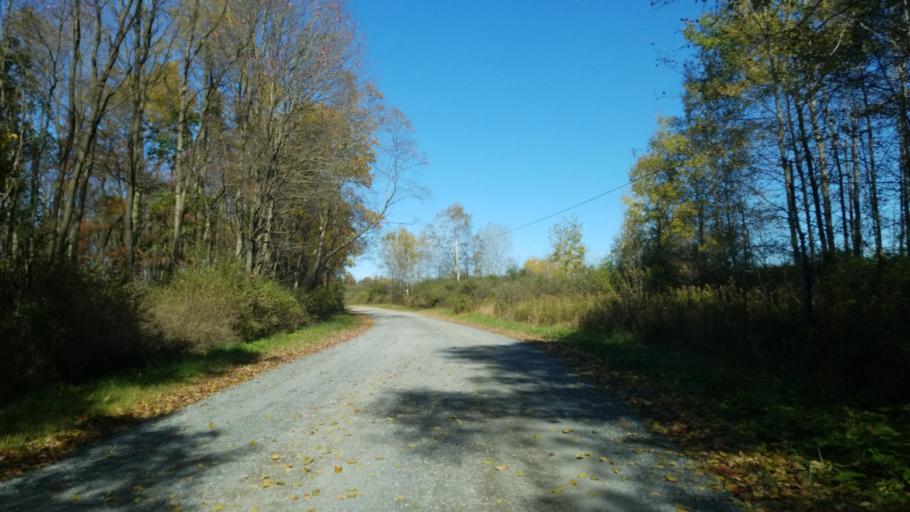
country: US
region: Pennsylvania
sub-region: Jefferson County
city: Falls Creek
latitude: 41.1800
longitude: -78.7832
